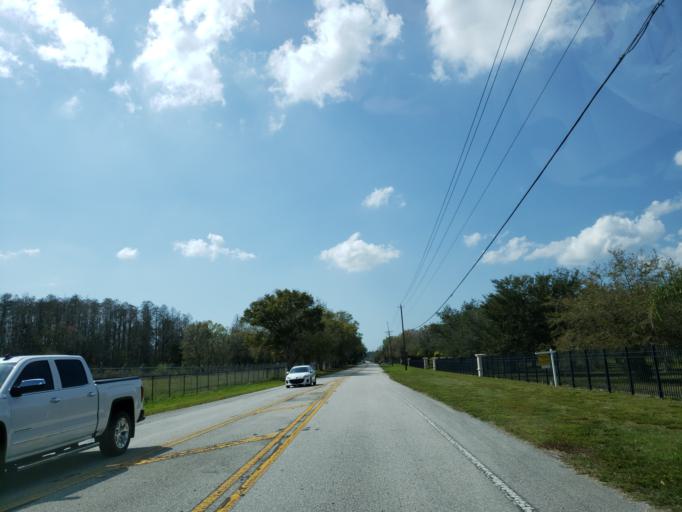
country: US
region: Florida
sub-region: Hillsborough County
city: Keystone
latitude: 28.1442
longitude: -82.6057
